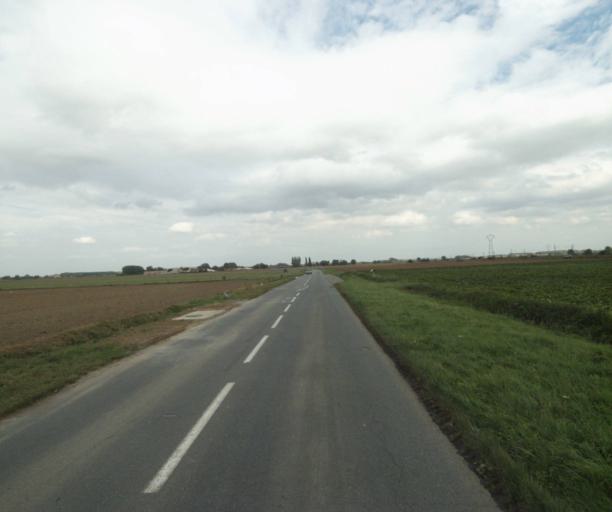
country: FR
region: Nord-Pas-de-Calais
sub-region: Departement du Nord
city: Salome
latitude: 50.5431
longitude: 2.8390
